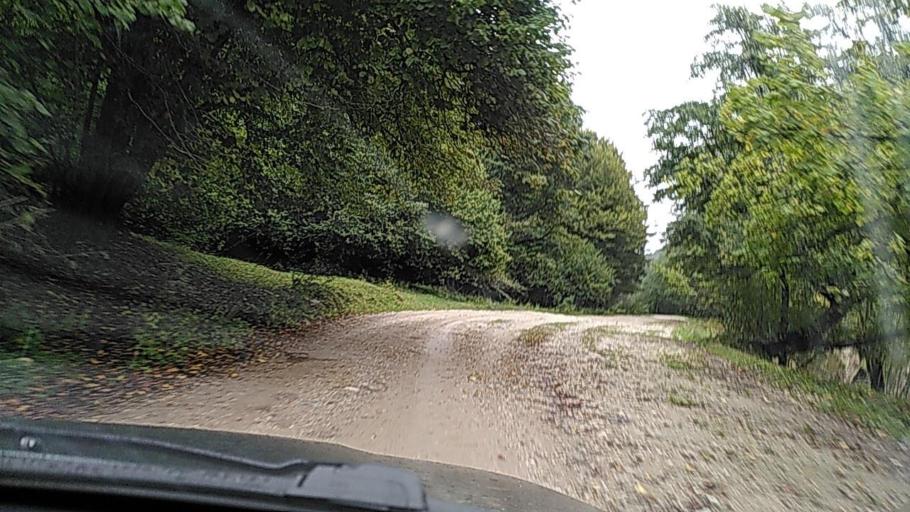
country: RU
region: Kabardino-Balkariya
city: Belaya Rechka
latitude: 43.4130
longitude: 43.4731
